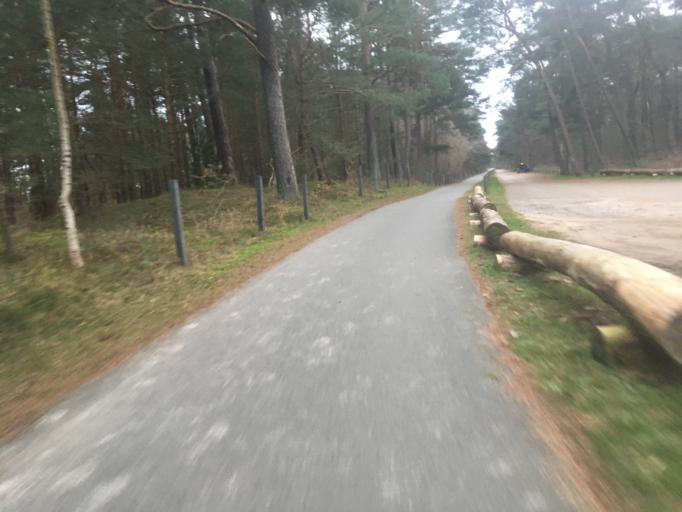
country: DE
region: Mecklenburg-Vorpommern
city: Sagard
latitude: 54.4708
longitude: 13.5684
